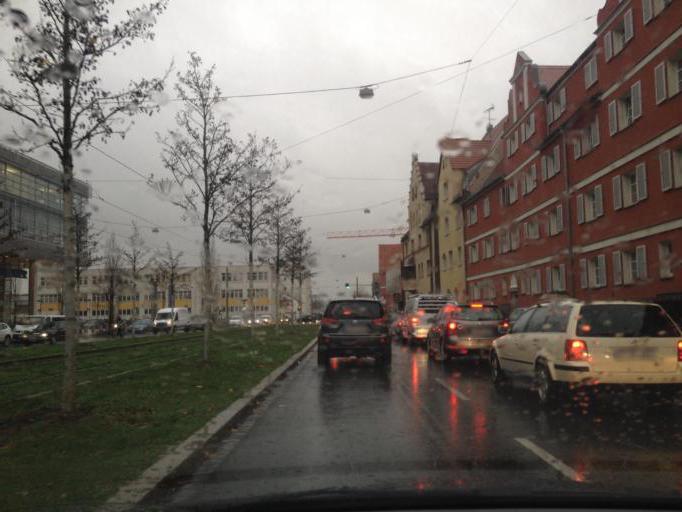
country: DE
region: Bavaria
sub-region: Regierungsbezirk Mittelfranken
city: Nuernberg
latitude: 49.4554
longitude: 11.1175
